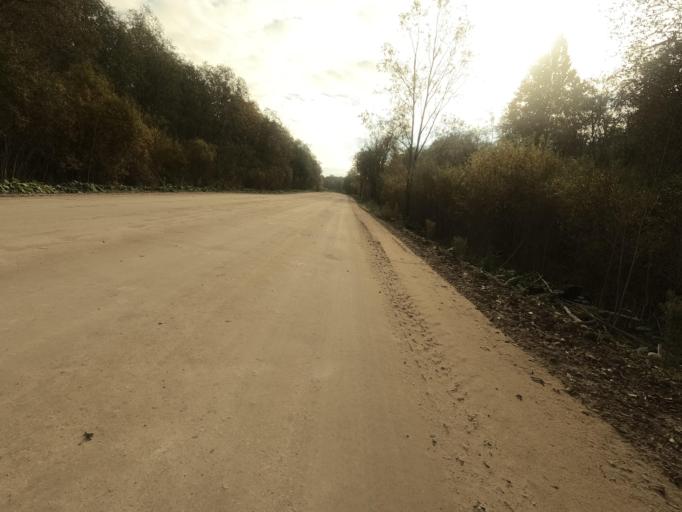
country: RU
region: Novgorod
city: Batetskiy
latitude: 58.7995
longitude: 30.6328
